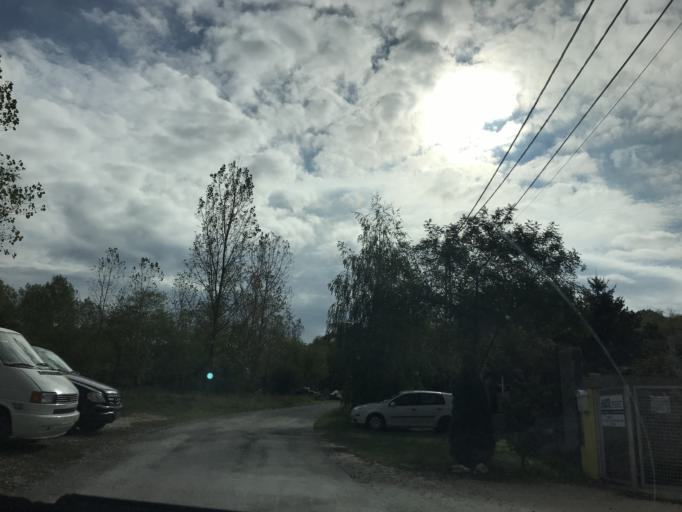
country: HU
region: Komarom-Esztergom
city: Piliscsev
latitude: 47.6718
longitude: 18.7954
